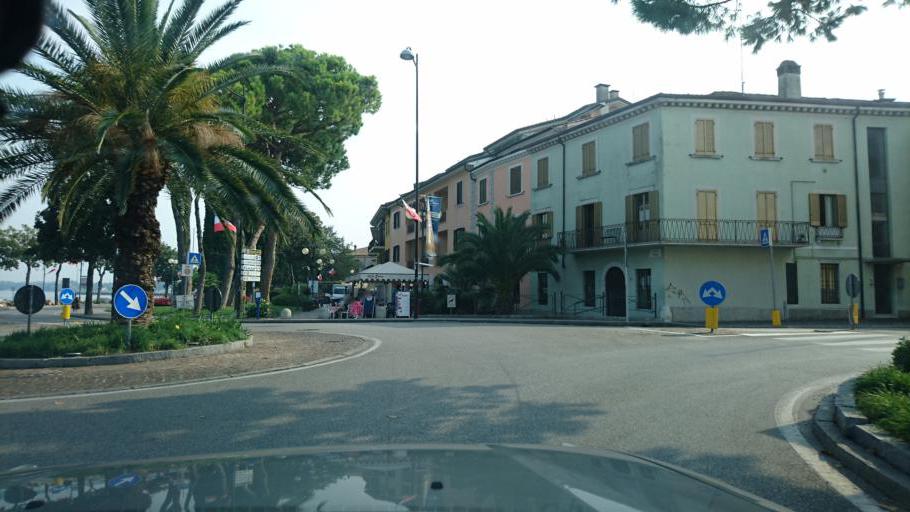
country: IT
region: Lombardy
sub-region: Provincia di Brescia
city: Desenzano del Garda
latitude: 45.4745
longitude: 10.5386
